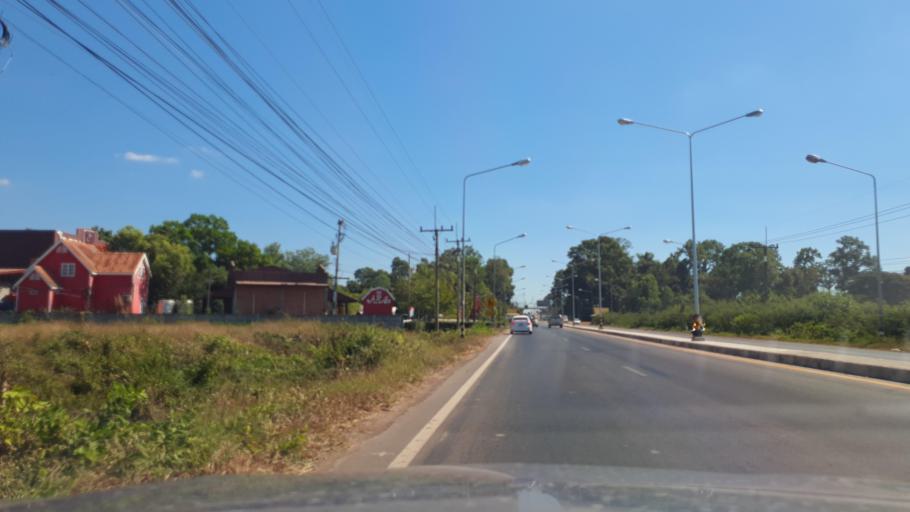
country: TH
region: Sakon Nakhon
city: Sakon Nakhon
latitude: 17.0866
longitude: 104.1843
